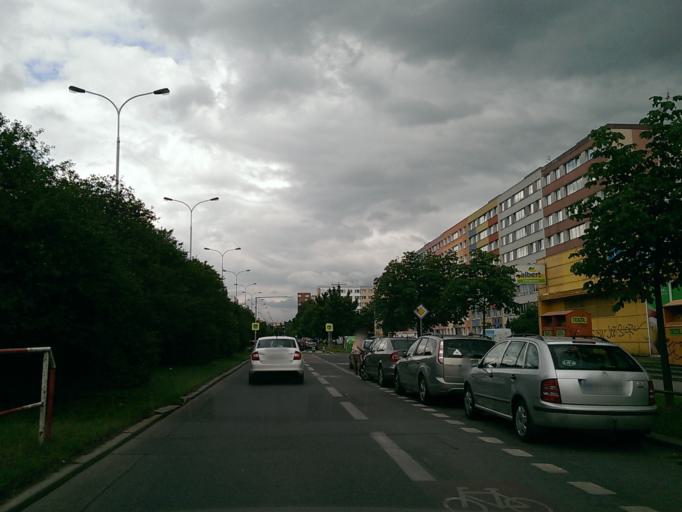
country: CZ
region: Praha
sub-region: Praha 4
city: Hodkovicky
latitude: 50.0249
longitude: 14.4347
